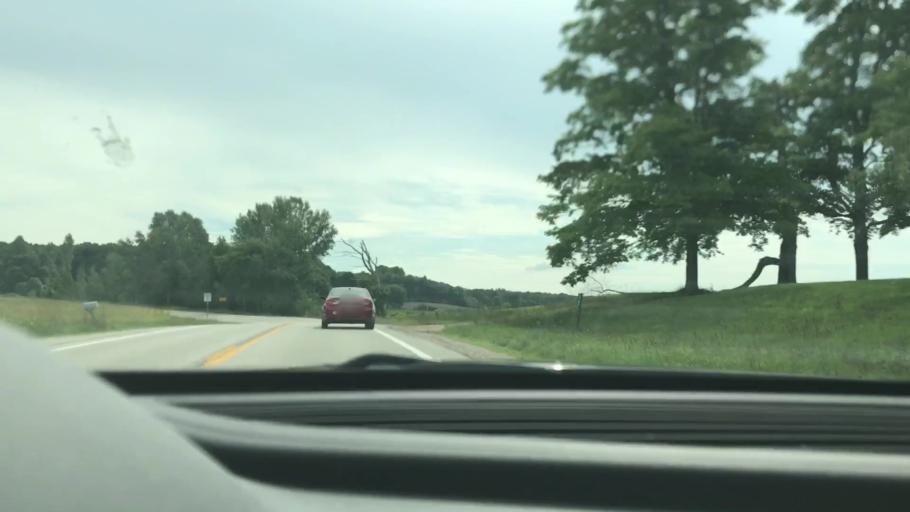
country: US
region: Michigan
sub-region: Antrim County
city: Bellaire
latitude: 45.0872
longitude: -85.2899
